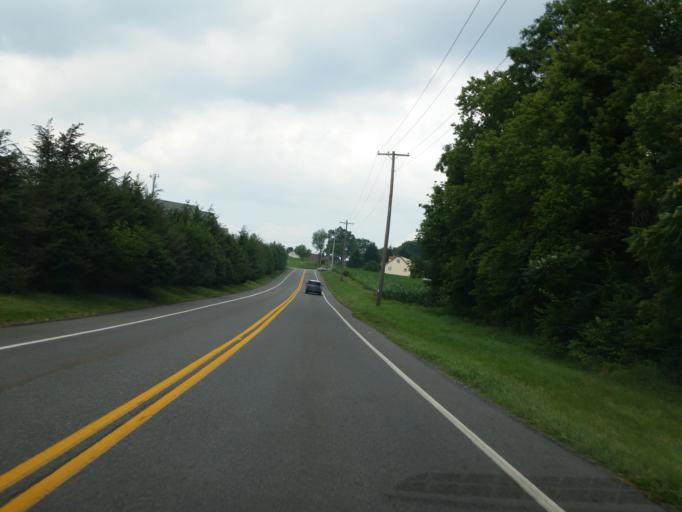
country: US
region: Pennsylvania
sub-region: Lebanon County
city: Palmyra
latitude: 40.3203
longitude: -76.5908
